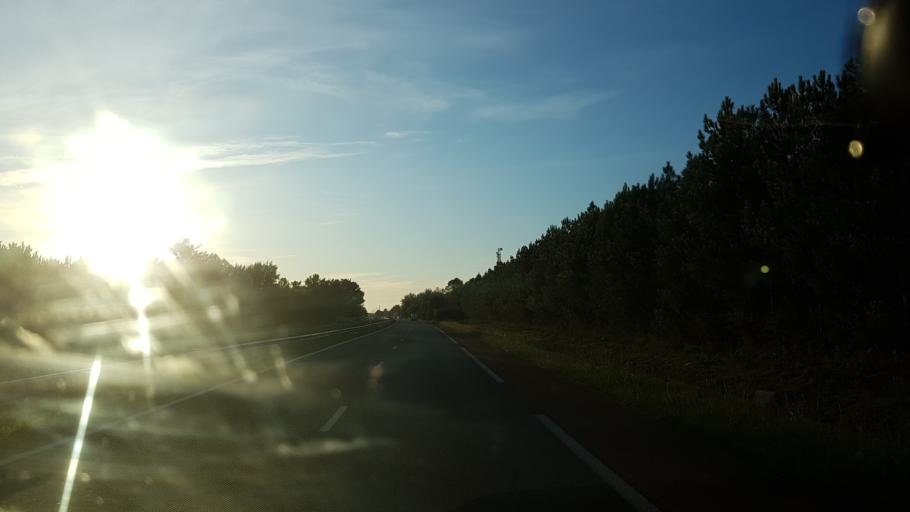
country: FR
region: Aquitaine
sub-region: Departement de la Gironde
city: Andernos-les-Bains
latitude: 44.7778
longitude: -1.0400
